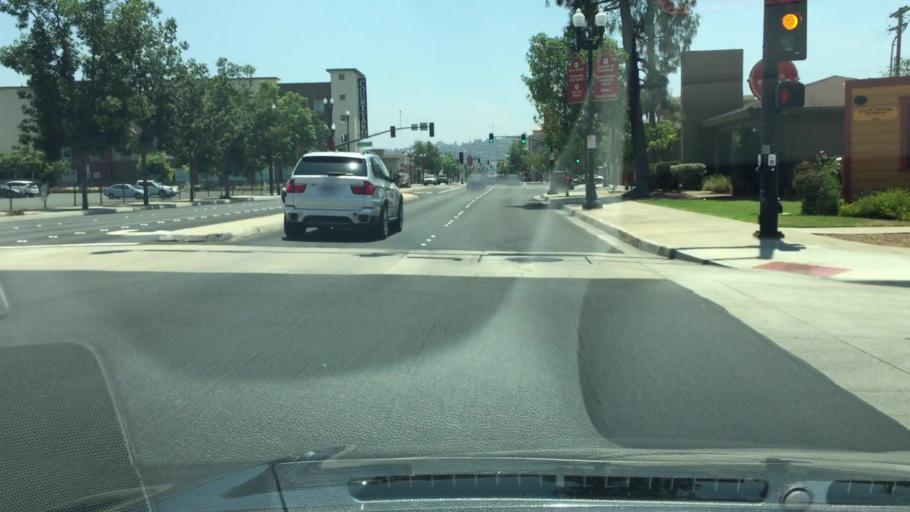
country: US
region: California
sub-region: San Diego County
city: El Cajon
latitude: 32.7975
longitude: -116.9624
